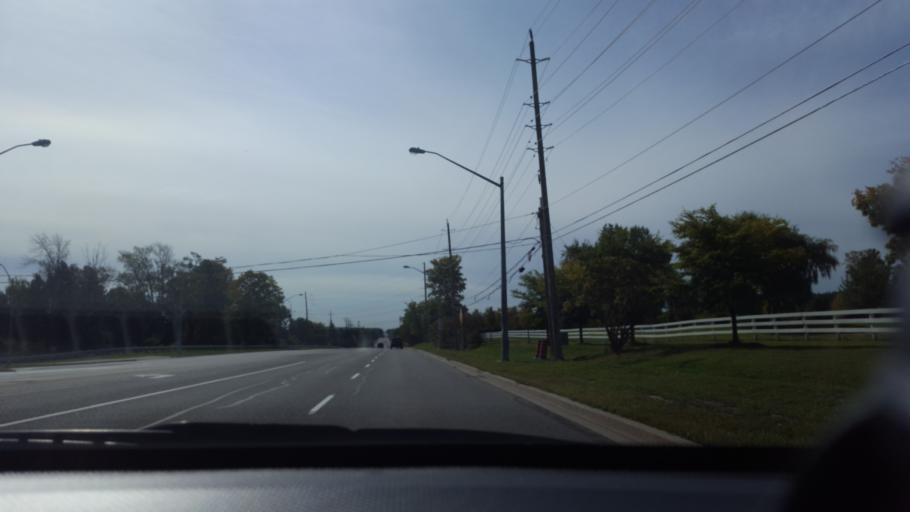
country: CA
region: Ontario
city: Newmarket
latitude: 44.0026
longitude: -79.4963
